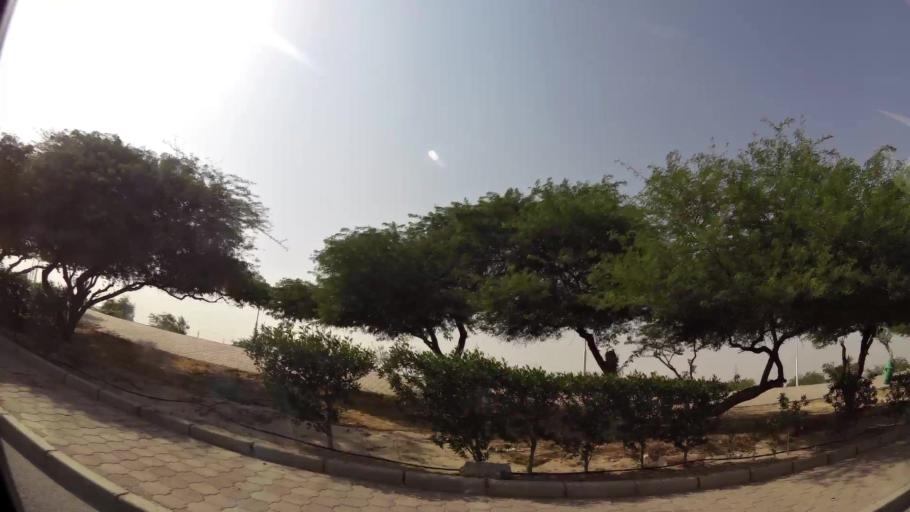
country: KW
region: Muhafazat al Jahra'
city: Al Jahra'
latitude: 29.3290
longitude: 47.6471
